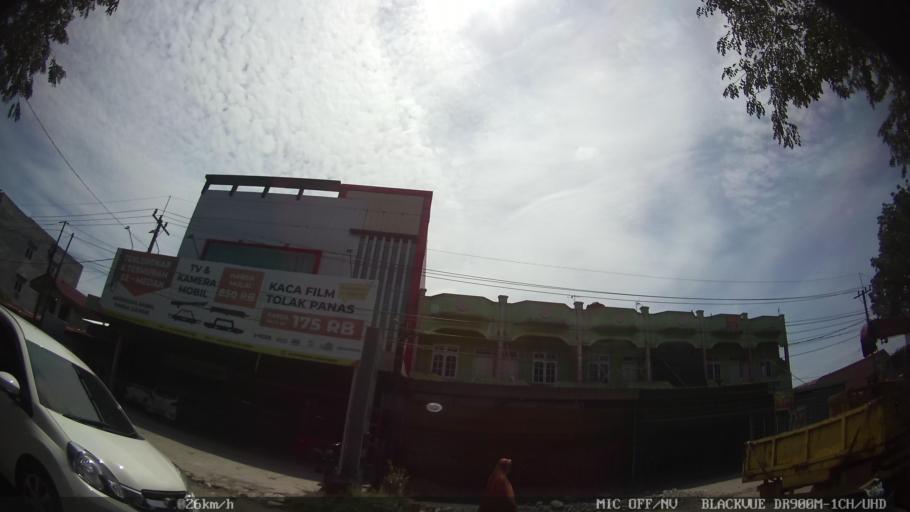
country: ID
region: North Sumatra
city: Sunggal
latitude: 3.5840
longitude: 98.6270
